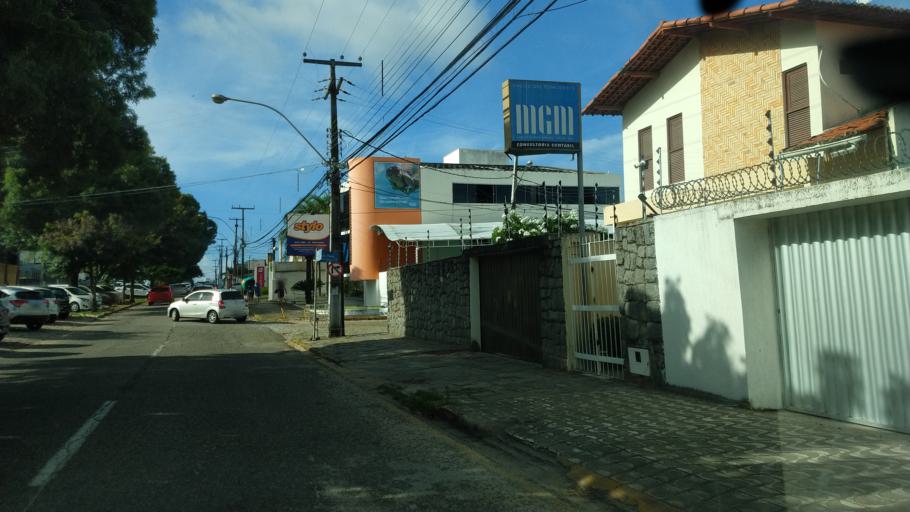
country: BR
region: Rio Grande do Norte
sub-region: Natal
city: Natal
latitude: -5.8121
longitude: -35.2016
